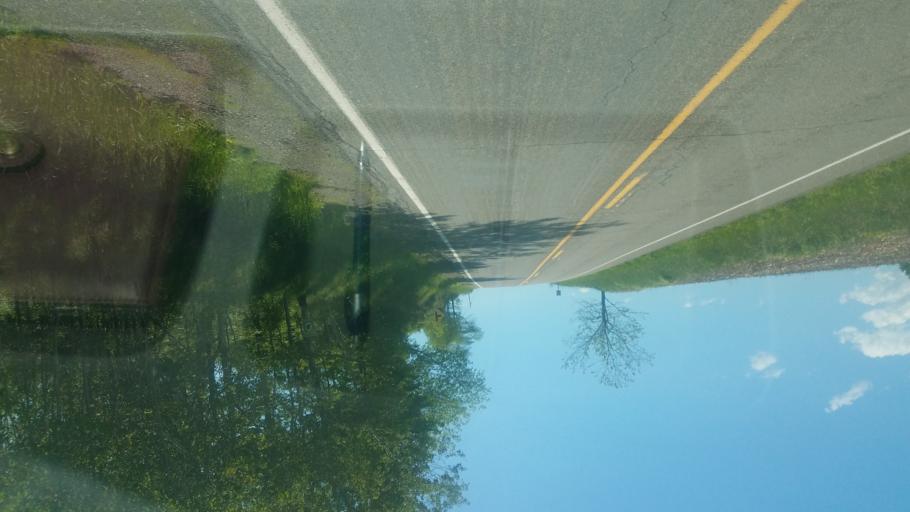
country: US
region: Pennsylvania
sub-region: Tioga County
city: Wellsboro
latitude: 41.7341
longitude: -77.3663
